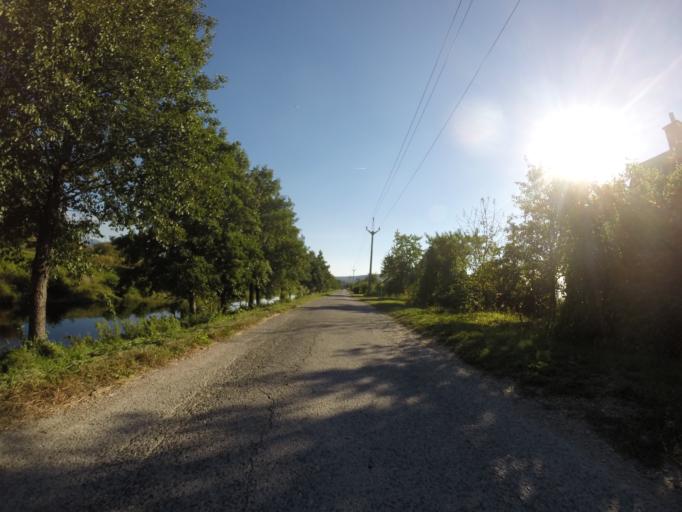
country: SK
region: Nitriansky
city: Novaky
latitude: 48.7196
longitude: 18.5321
